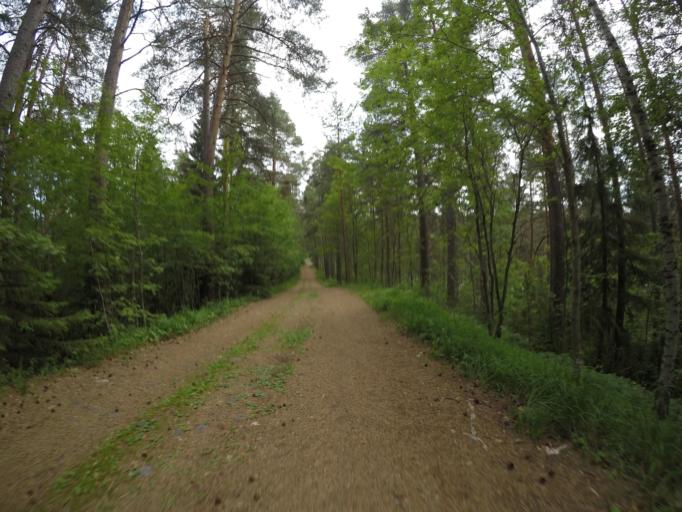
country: FI
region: Haeme
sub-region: Haemeenlinna
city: Haemeenlinna
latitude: 60.9944
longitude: 24.4219
